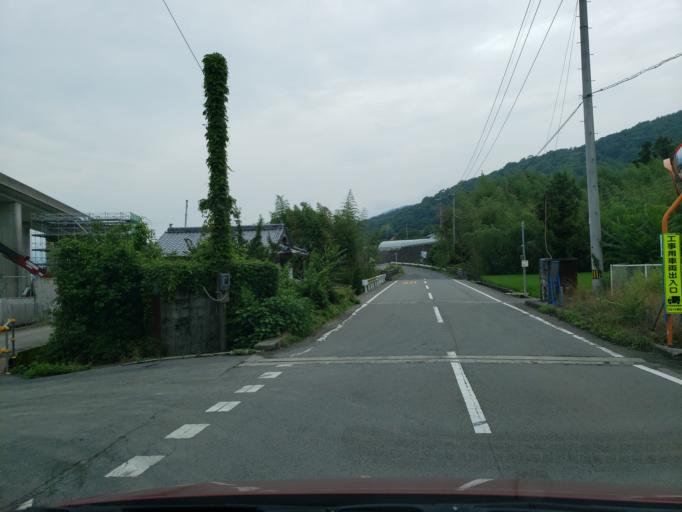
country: JP
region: Tokushima
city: Wakimachi
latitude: 34.1042
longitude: 134.2387
